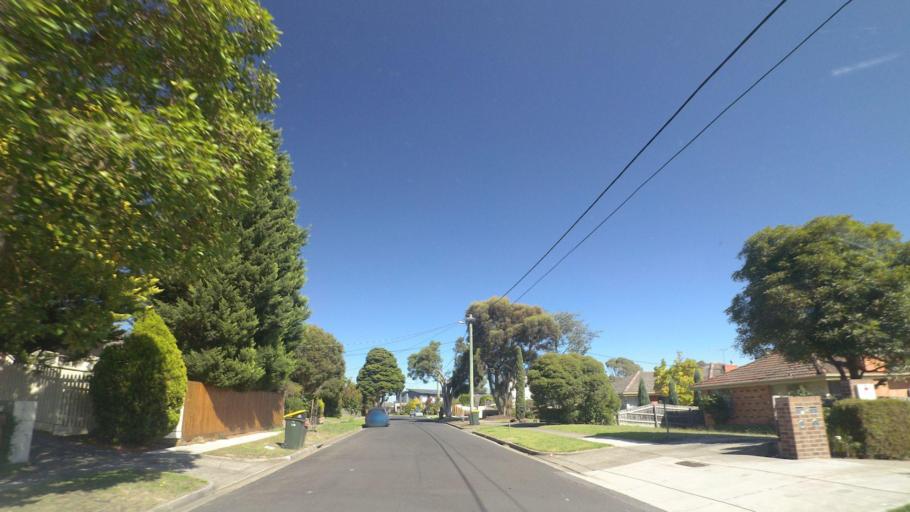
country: AU
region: Victoria
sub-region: Manningham
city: Donvale
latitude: -37.7988
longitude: 145.1681
